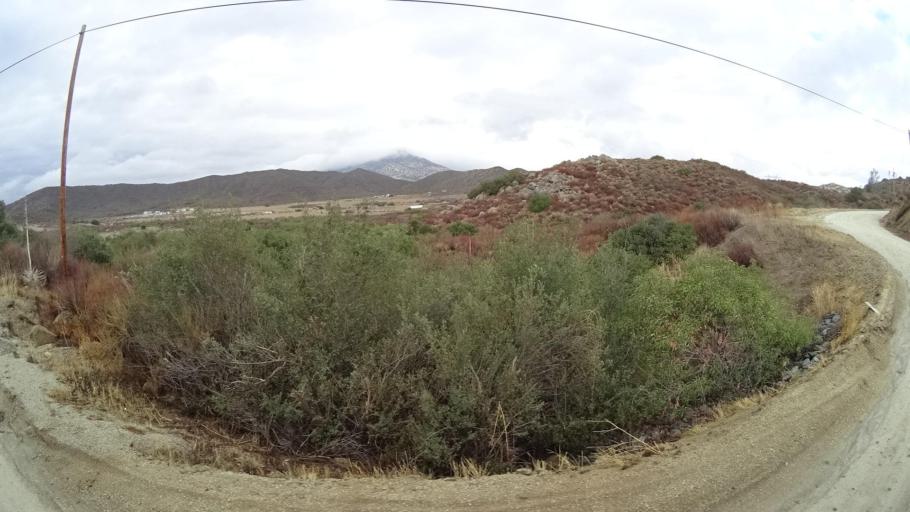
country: MX
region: Baja California
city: Tecate
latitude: 32.5949
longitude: -116.6346
